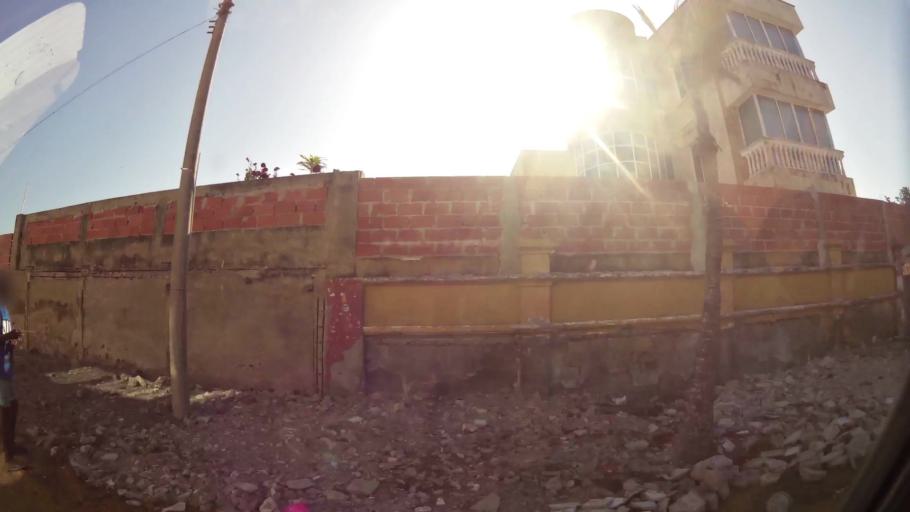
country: CO
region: Bolivar
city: Cartagena
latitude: 10.4856
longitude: -75.4914
